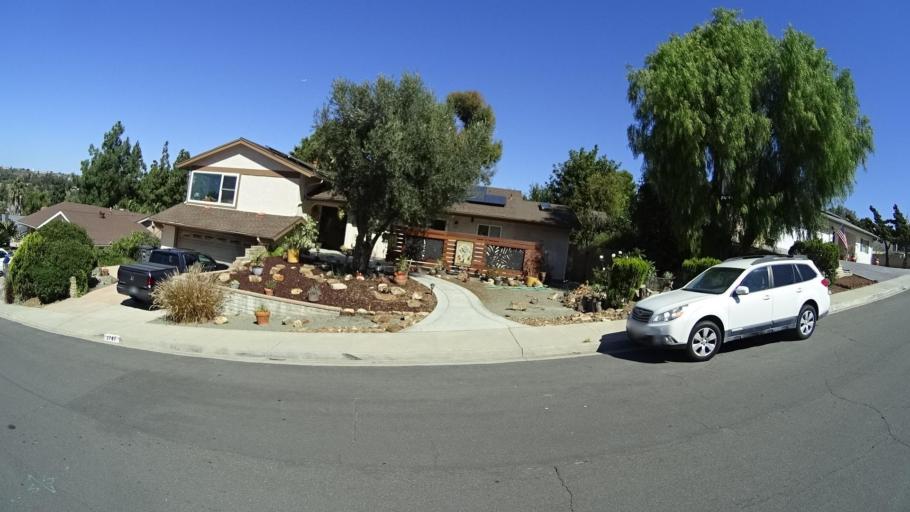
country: US
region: California
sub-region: San Diego County
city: Bonita
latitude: 32.6650
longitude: -117.0202
